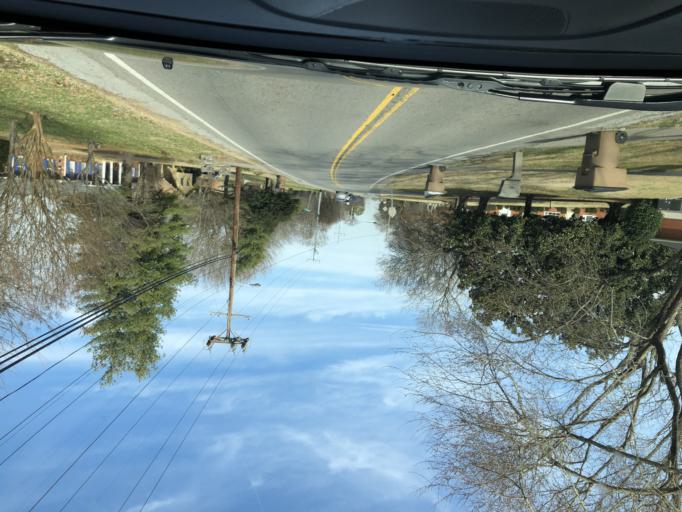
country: US
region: Tennessee
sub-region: Davidson County
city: Lakewood
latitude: 36.1961
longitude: -86.6734
